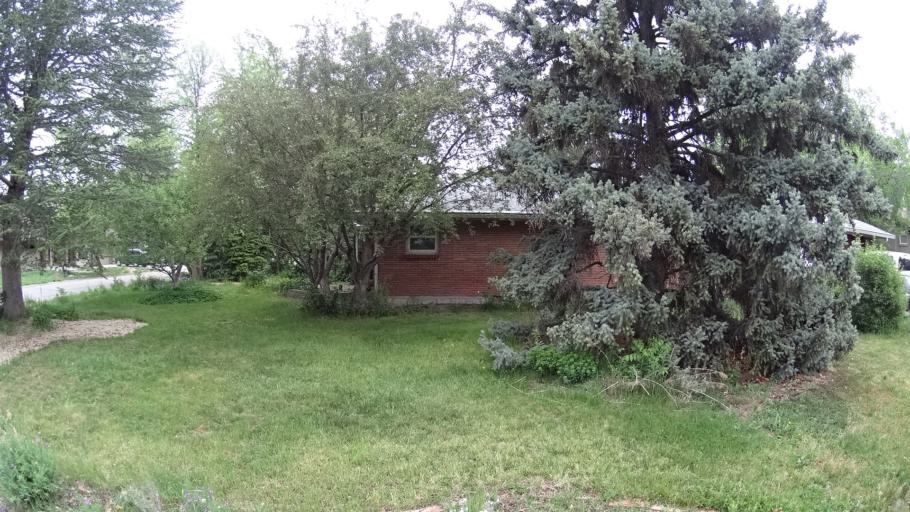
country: US
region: Idaho
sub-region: Ada County
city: Boise
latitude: 43.6110
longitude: -116.1791
